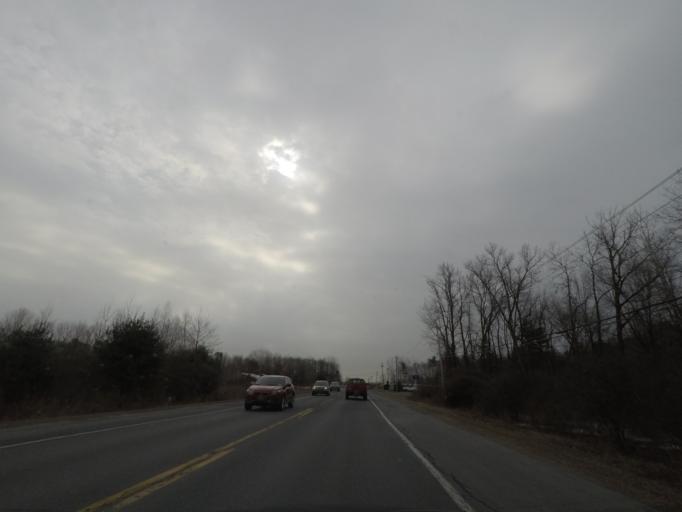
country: US
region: New York
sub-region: Warren County
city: Glens Falls
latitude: 43.3235
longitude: -73.6241
